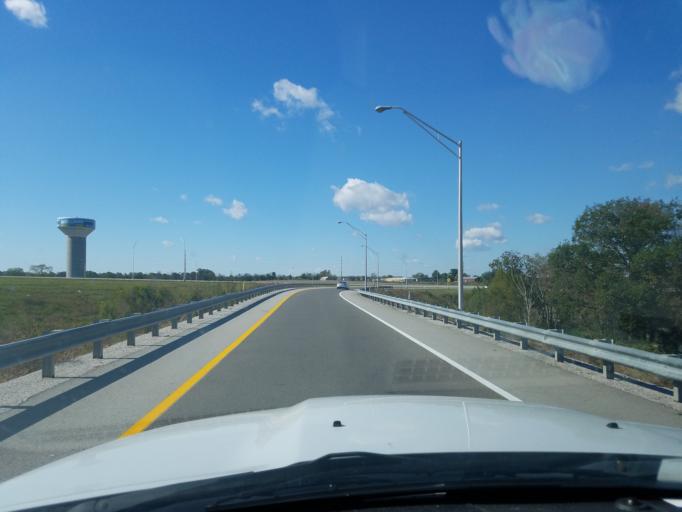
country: US
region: Kentucky
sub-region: Warren County
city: Plano
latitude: 36.9123
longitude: -86.4334
